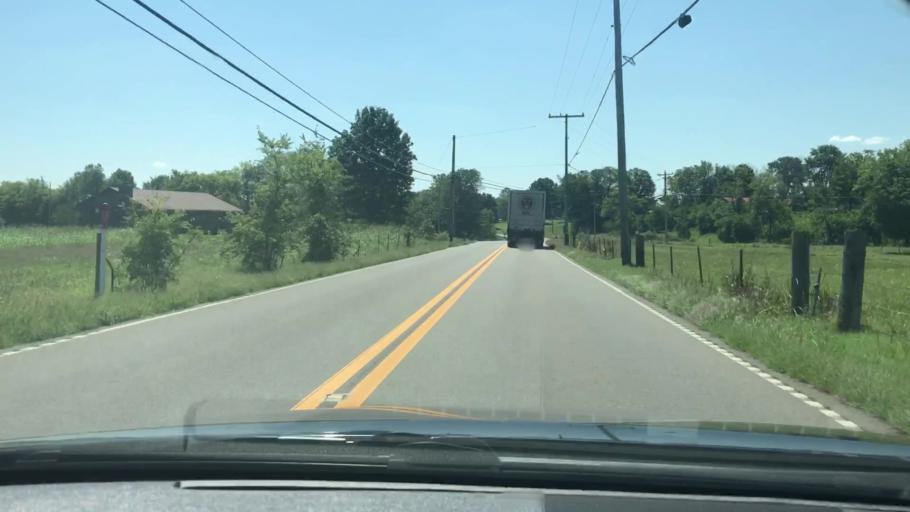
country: US
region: Tennessee
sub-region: Sumner County
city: Gallatin
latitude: 36.4228
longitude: -86.5180
